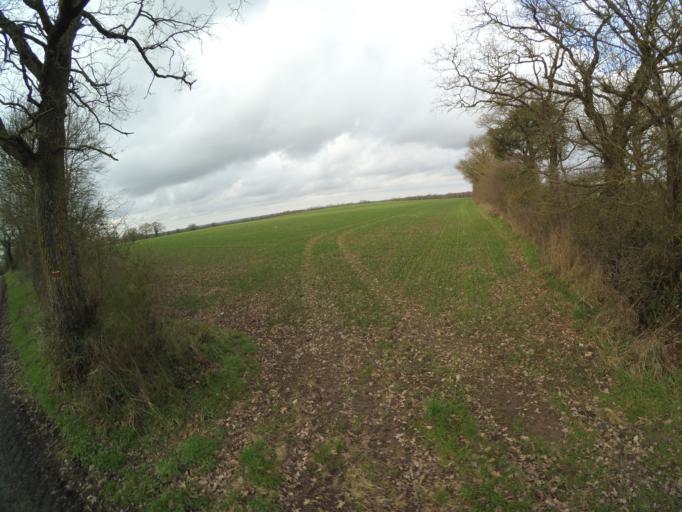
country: FR
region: Pays de la Loire
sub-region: Departement de la Vendee
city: La Bernardiere
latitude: 47.0215
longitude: -1.2924
